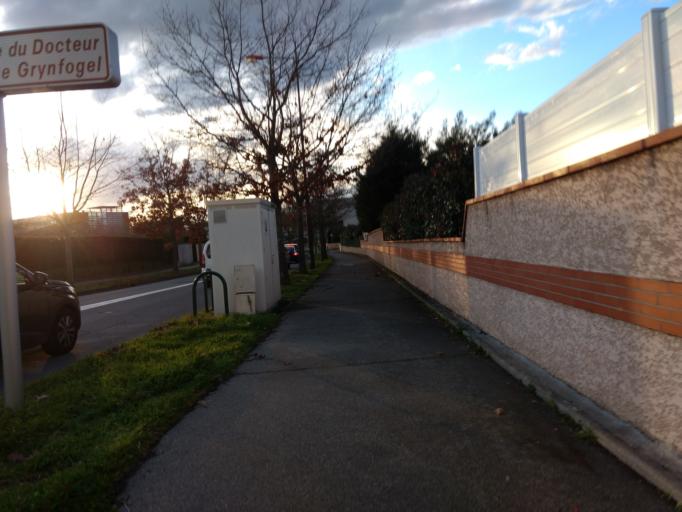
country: FR
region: Midi-Pyrenees
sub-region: Departement de la Haute-Garonne
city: Colomiers
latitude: 43.5804
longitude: 1.3701
